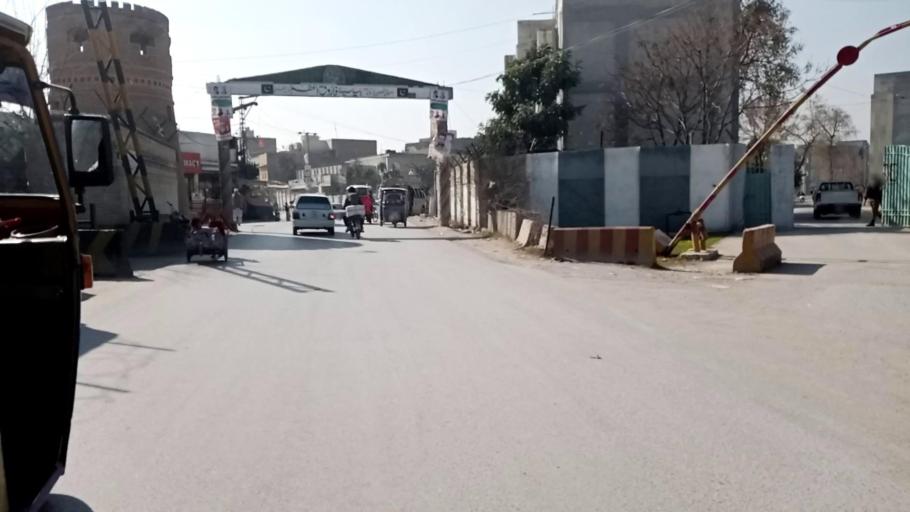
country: PK
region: Khyber Pakhtunkhwa
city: Peshawar
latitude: 33.9848
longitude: 71.5305
